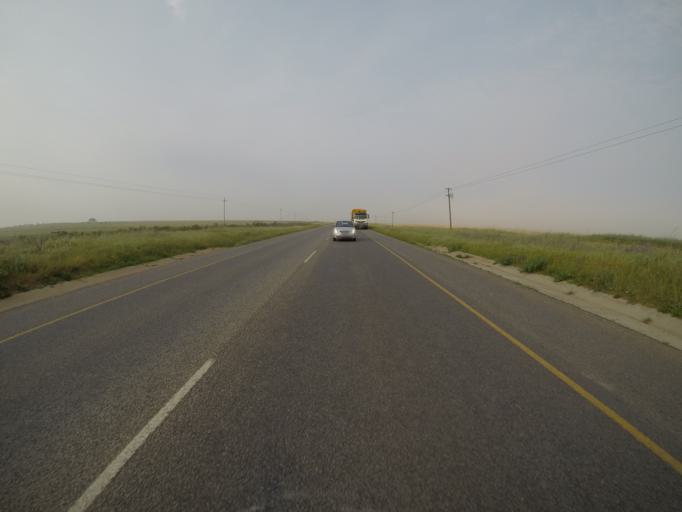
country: ZA
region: Western Cape
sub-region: West Coast District Municipality
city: Malmesbury
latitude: -33.6509
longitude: 18.7104
